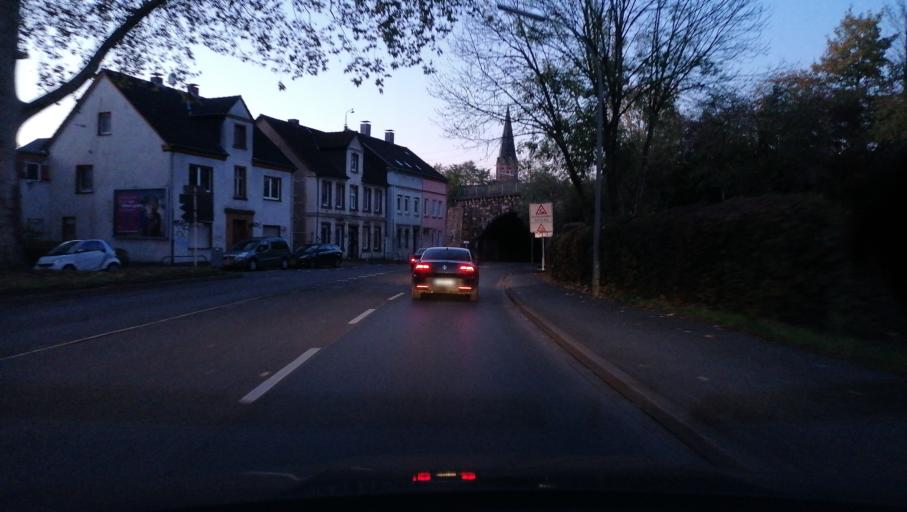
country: DE
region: North Rhine-Westphalia
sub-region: Regierungsbezirk Arnsberg
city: Dortmund
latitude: 51.4863
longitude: 7.5058
